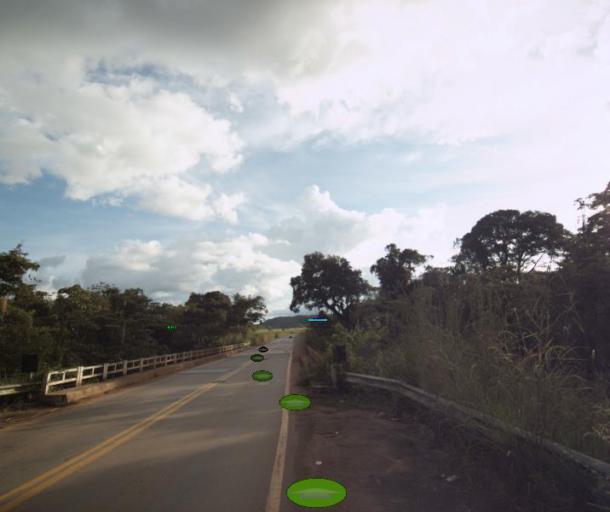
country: BR
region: Goias
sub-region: Niquelandia
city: Niquelandia
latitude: -14.5365
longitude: -48.5405
